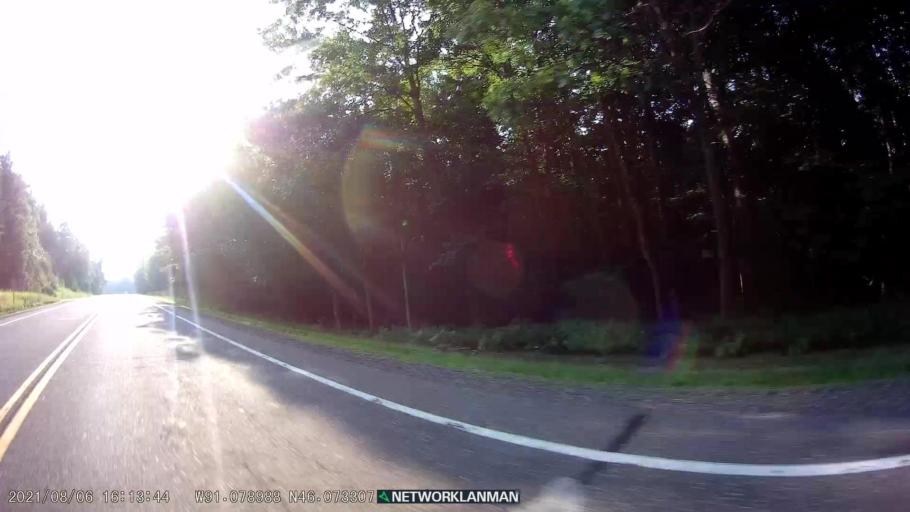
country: US
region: Wisconsin
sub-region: Sawyer County
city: Little Round Lake
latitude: 46.0733
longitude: -91.0792
